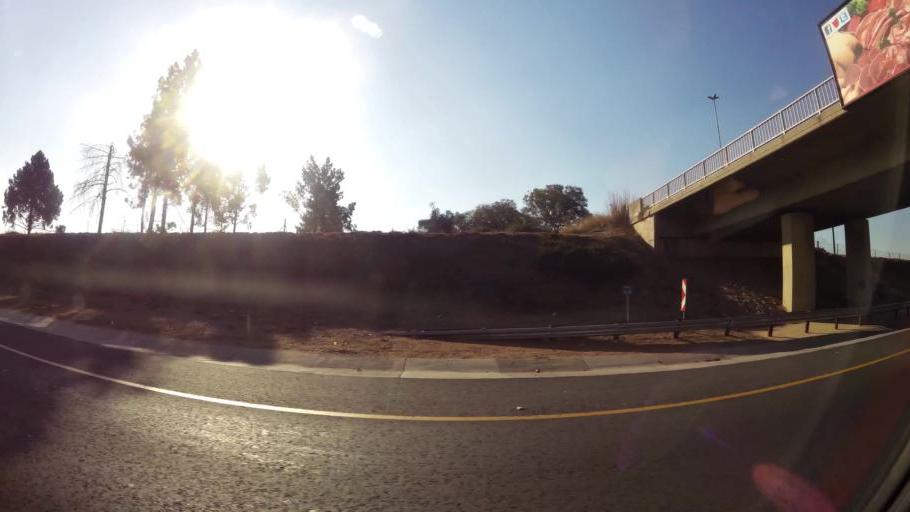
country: ZA
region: Gauteng
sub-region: West Rand District Municipality
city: Muldersdriseloop
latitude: -26.0122
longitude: 27.8805
